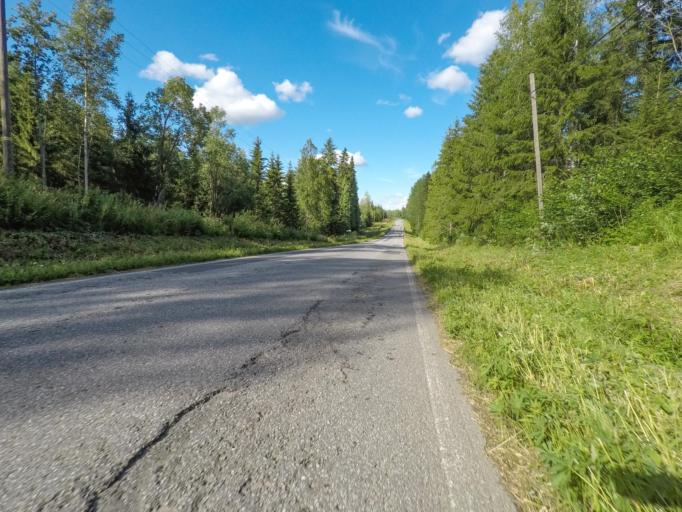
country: FI
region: South Karelia
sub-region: Imatra
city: Imatra
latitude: 61.1353
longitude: 28.7326
